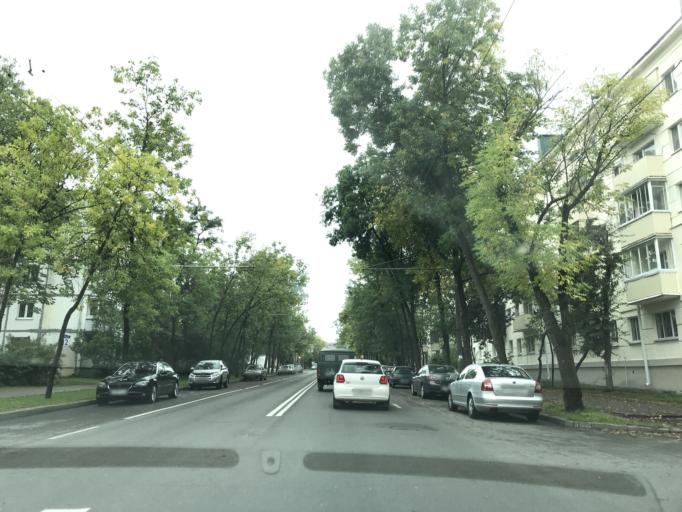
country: BY
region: Minsk
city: Minsk
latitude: 53.9344
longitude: 27.6128
